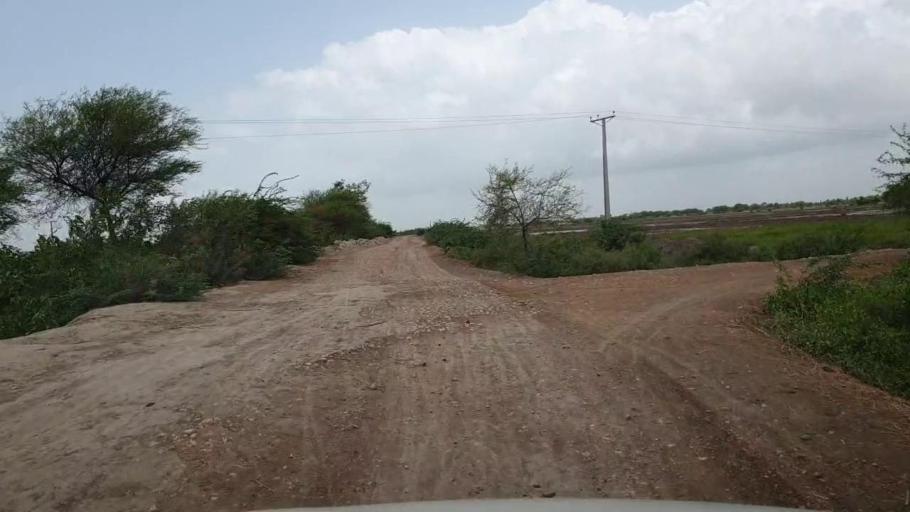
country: PK
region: Sindh
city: Kario
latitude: 24.6919
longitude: 68.6587
